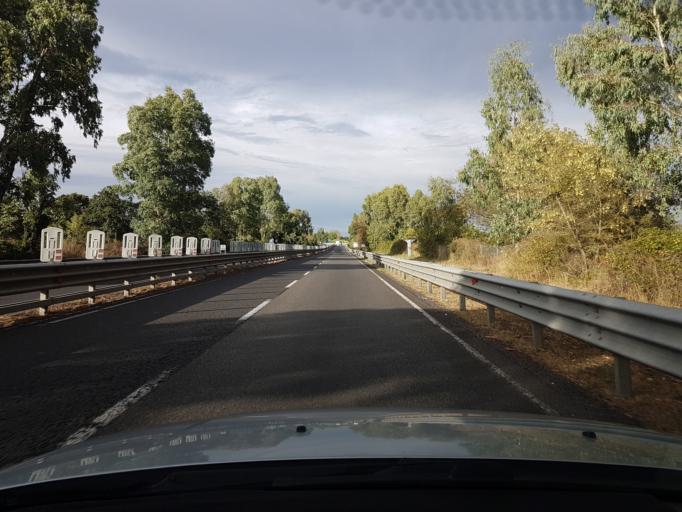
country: IT
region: Sardinia
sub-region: Provincia di Oristano
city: Paulilatino
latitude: 40.1047
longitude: 8.7886
